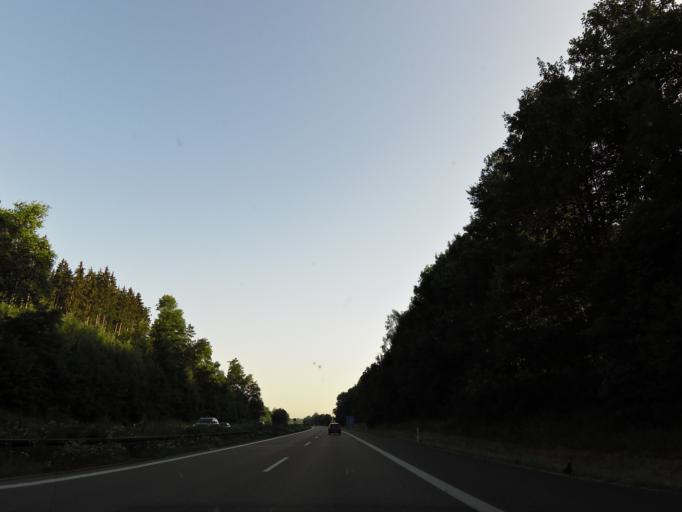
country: DE
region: Bavaria
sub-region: Swabia
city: Illertissen
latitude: 48.2361
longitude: 10.1226
